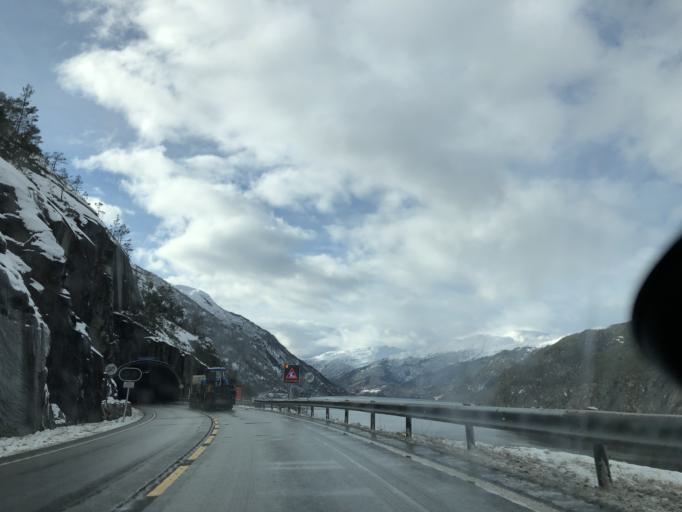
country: NO
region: Rogaland
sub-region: Sauda
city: Sauda
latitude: 59.8459
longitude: 6.3360
